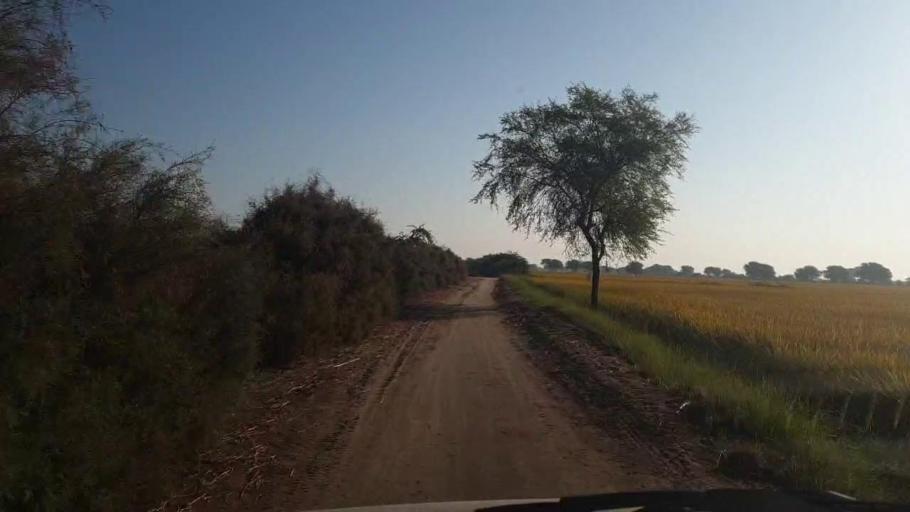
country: PK
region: Sindh
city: Talhar
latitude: 24.8029
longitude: 68.8218
